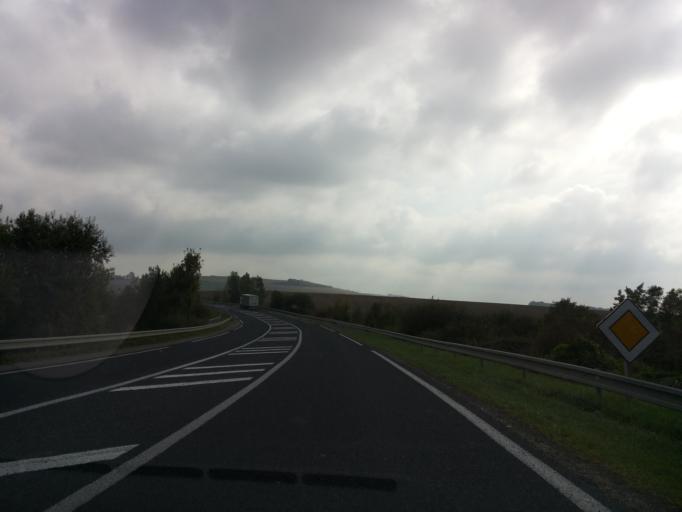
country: FR
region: Lorraine
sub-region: Departement de la Moselle
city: Solgne
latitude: 48.9494
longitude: 6.3075
